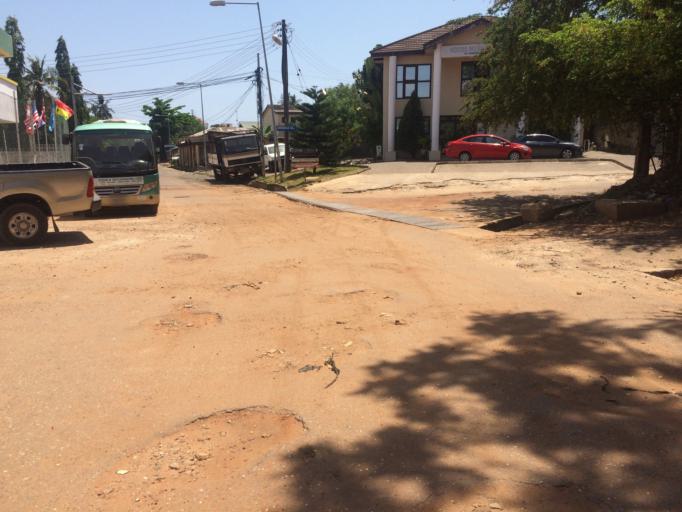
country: GH
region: Greater Accra
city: Accra
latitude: 5.5691
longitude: -0.1858
